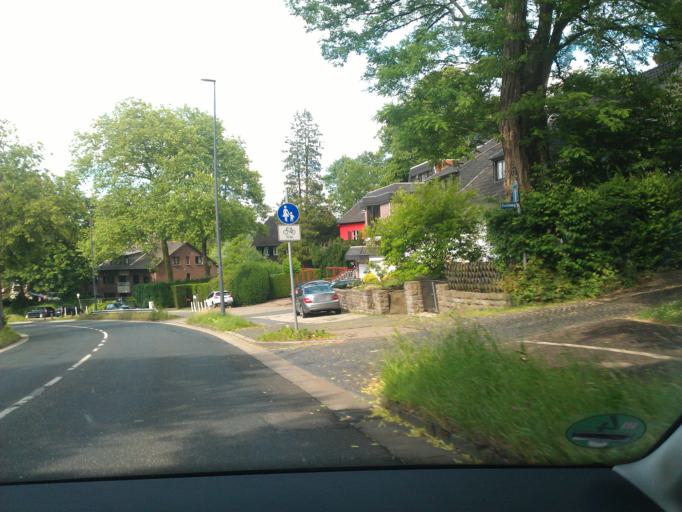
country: DE
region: North Rhine-Westphalia
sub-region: Regierungsbezirk Koln
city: Aachen
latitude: 50.7443
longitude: 6.0877
